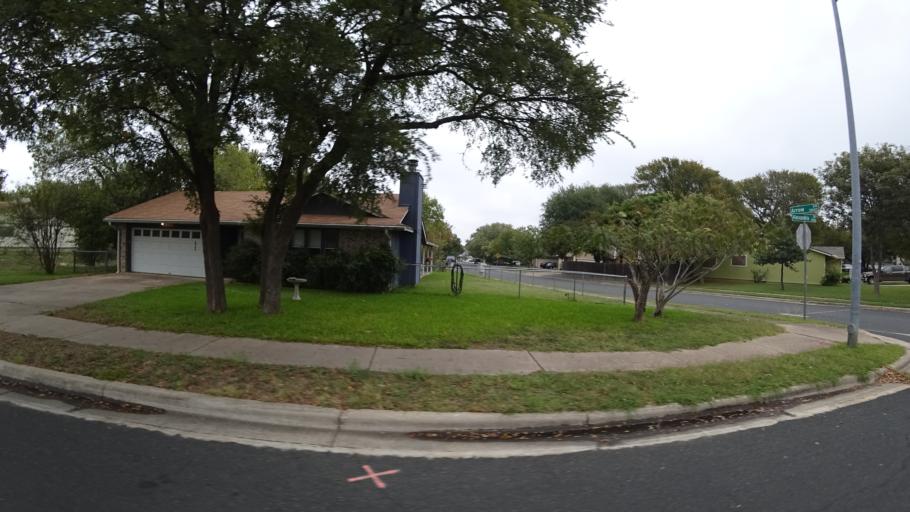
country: US
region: Texas
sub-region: Travis County
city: Shady Hollow
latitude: 30.2017
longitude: -97.8444
